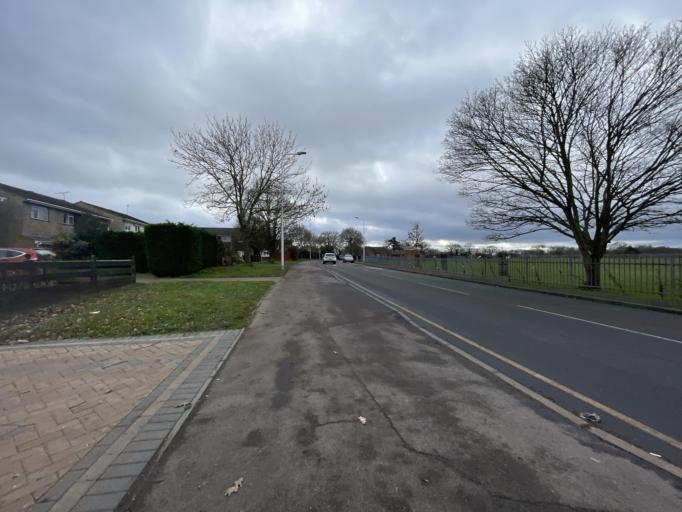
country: GB
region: England
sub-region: West Berkshire
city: Calcot
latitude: 51.4519
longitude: -1.0600
